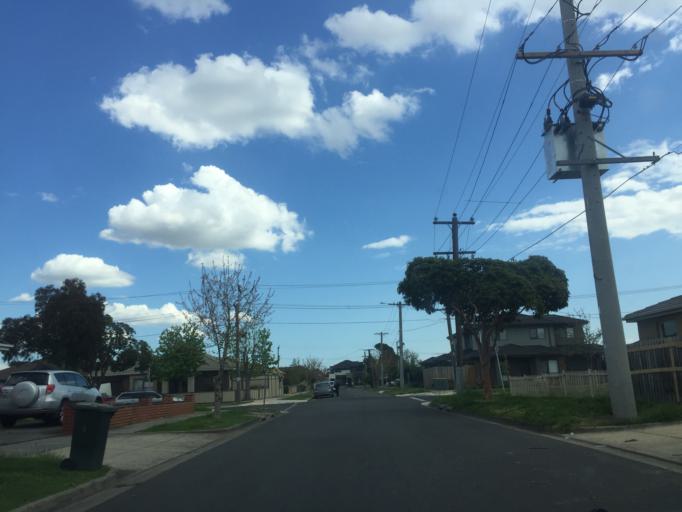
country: AU
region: Victoria
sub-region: Darebin
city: Kingsbury
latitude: -37.7168
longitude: 145.0394
